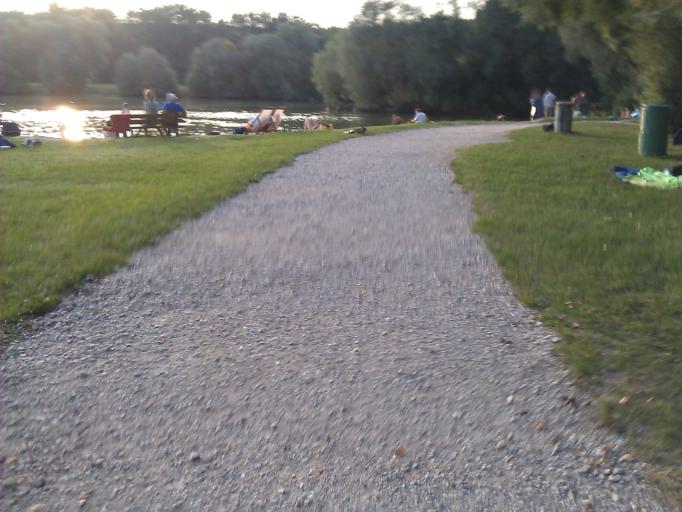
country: DE
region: Baden-Wuerttemberg
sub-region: Regierungsbezirk Stuttgart
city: Neckartailfingen
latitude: 48.6031
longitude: 9.2646
